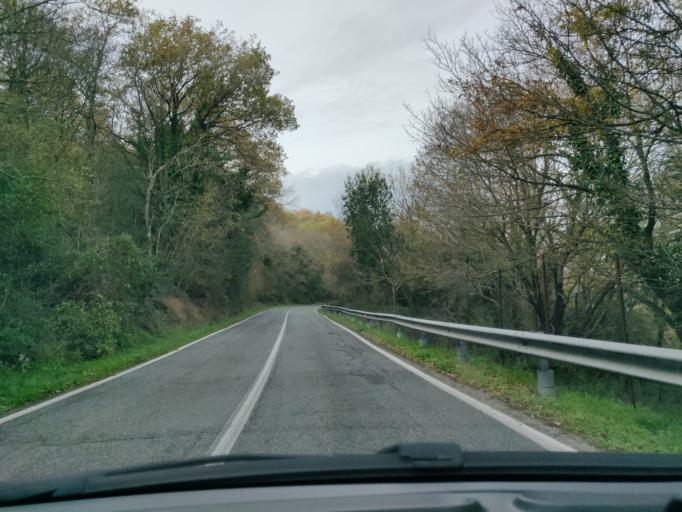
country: IT
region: Latium
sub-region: Citta metropolitana di Roma Capitale
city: Allumiere
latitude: 42.1452
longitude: 11.8918
